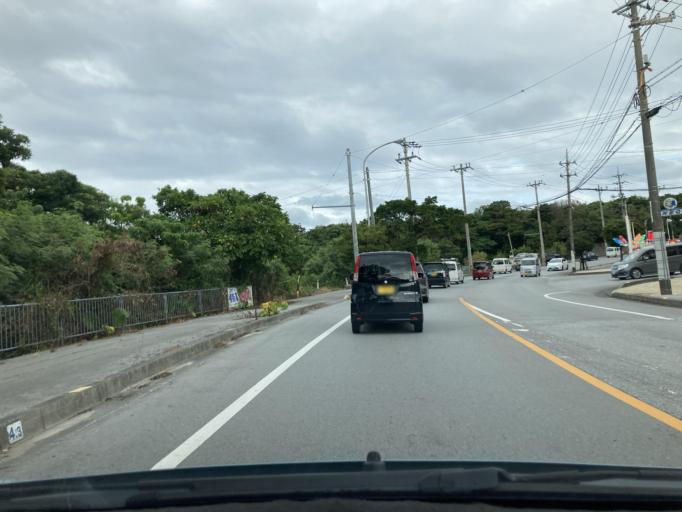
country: JP
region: Okinawa
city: Ginowan
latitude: 26.2454
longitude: 127.7635
